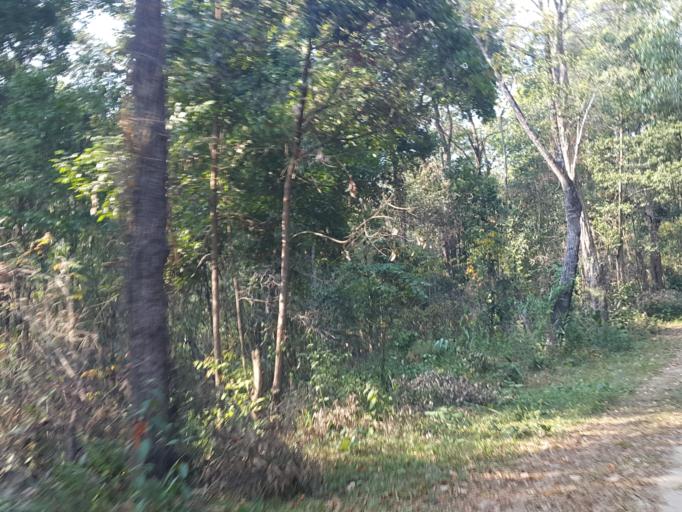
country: TH
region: Chiang Mai
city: Samoeng
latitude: 19.0225
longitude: 98.7615
